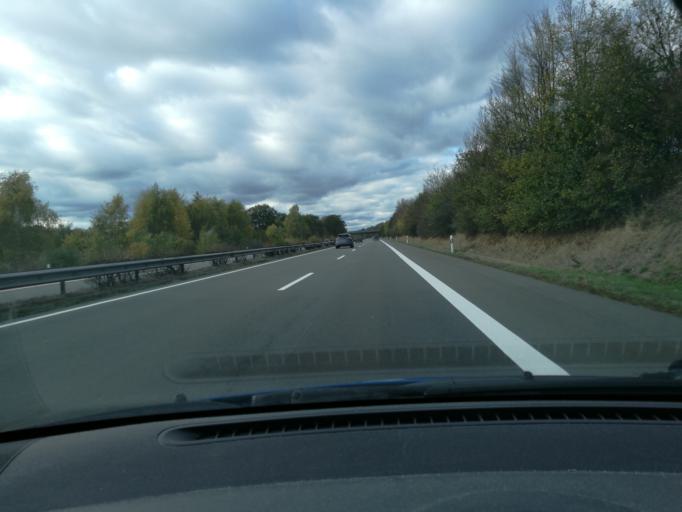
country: DE
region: Lower Saxony
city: Radbruch
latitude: 53.3211
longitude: 10.3042
